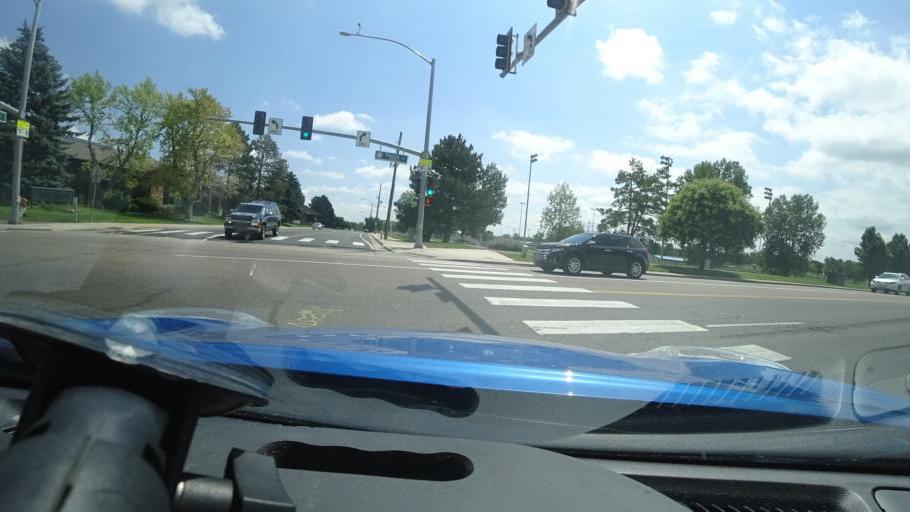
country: US
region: Colorado
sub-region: Adams County
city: Aurora
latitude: 39.7184
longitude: -104.8474
